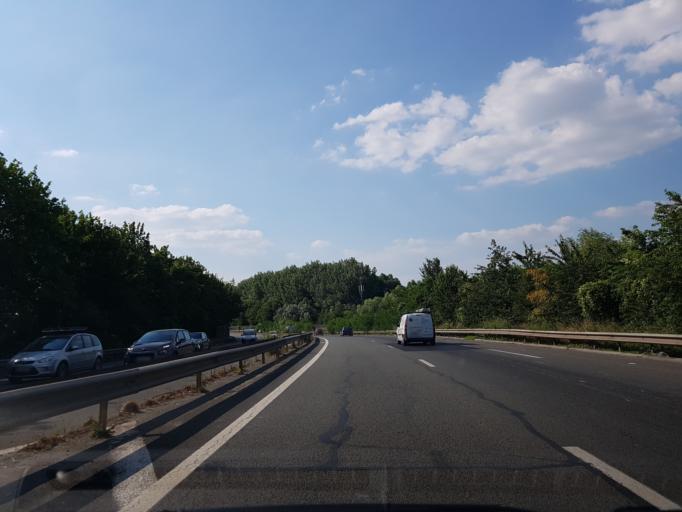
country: FR
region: Nord-Pas-de-Calais
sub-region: Departement du Nord
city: Waziers
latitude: 50.3885
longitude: 3.1287
